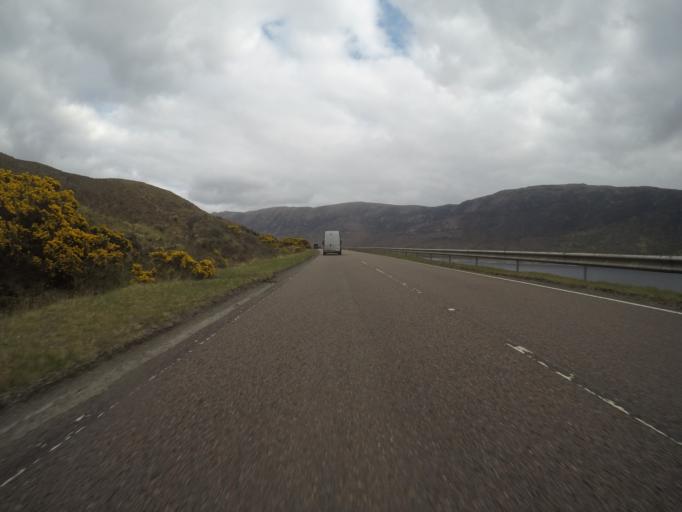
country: GB
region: Scotland
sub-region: Highland
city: Spean Bridge
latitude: 57.1450
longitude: -5.0901
